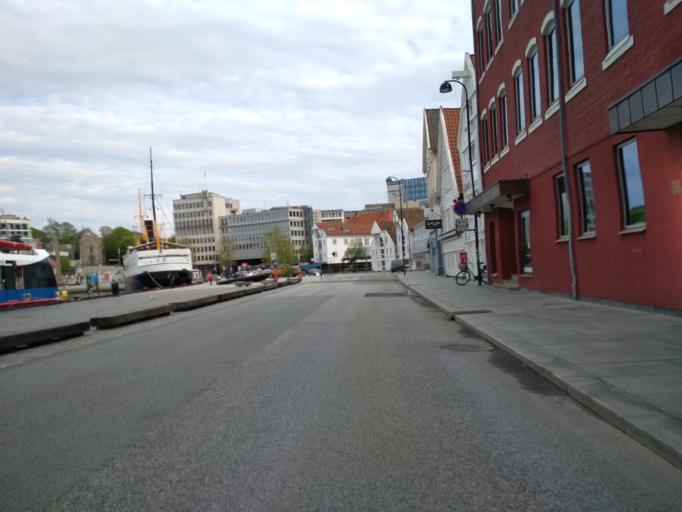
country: NO
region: Rogaland
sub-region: Stavanger
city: Stavanger
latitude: 58.9714
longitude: 5.7281
